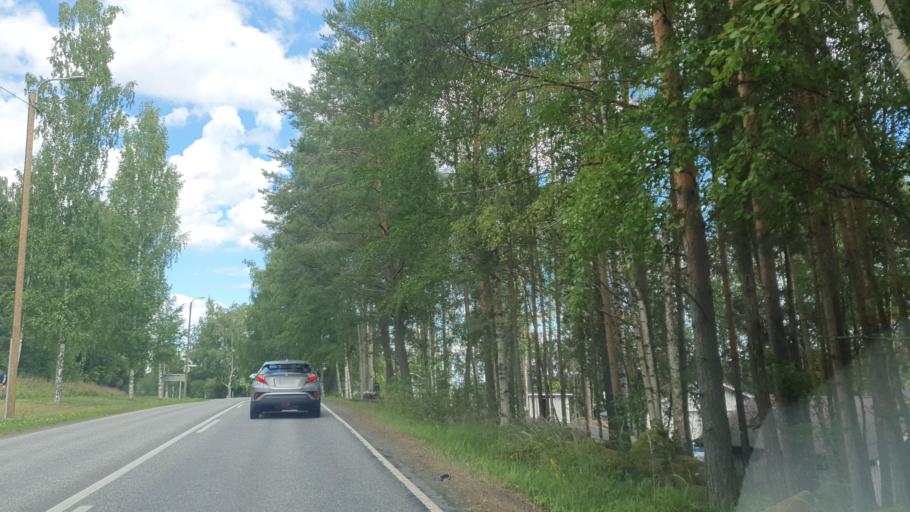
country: FI
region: Central Finland
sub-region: Jyvaeskylae
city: Saeynaetsalo
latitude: 62.1445
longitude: 25.7461
